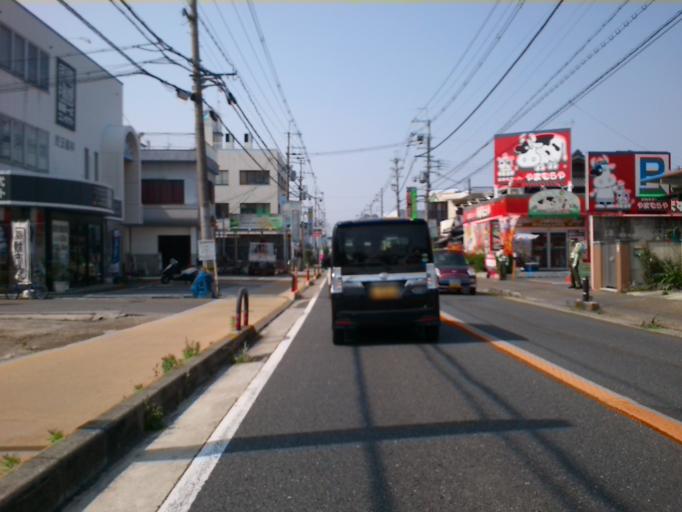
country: JP
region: Kyoto
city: Uji
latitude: 34.8966
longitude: 135.7833
